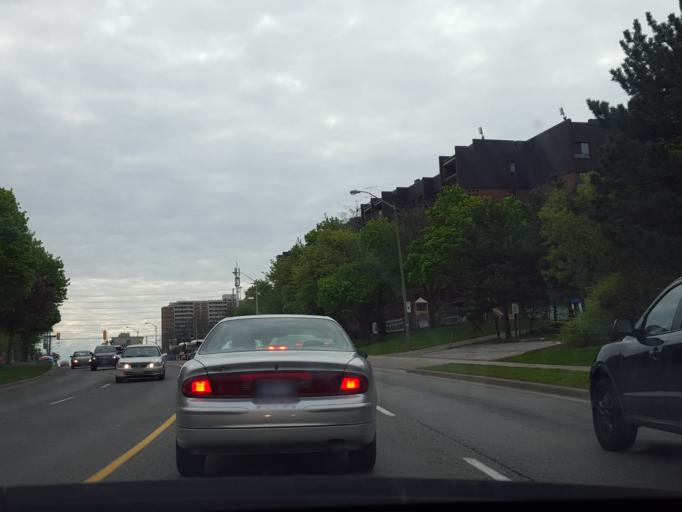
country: CA
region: Ontario
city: Willowdale
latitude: 43.7927
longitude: -79.3339
